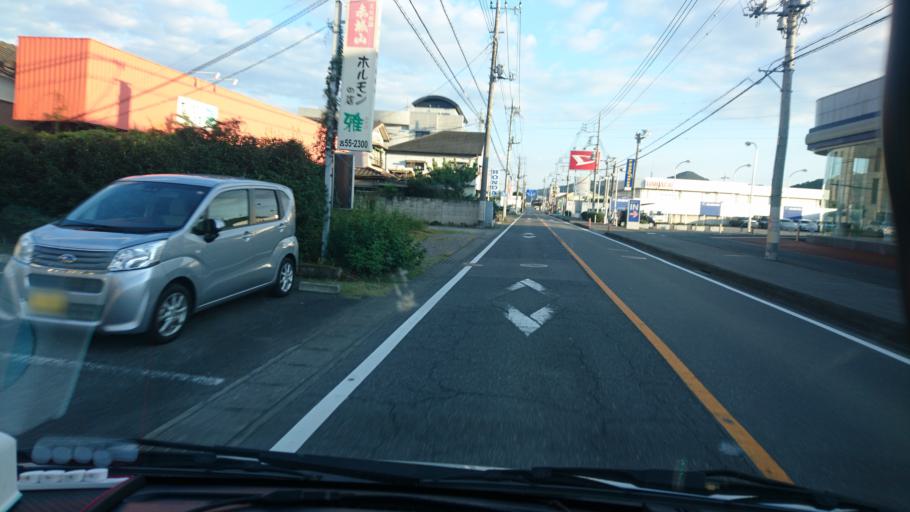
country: JP
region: Gunma
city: Kiryu
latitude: 36.3890
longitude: 139.3325
